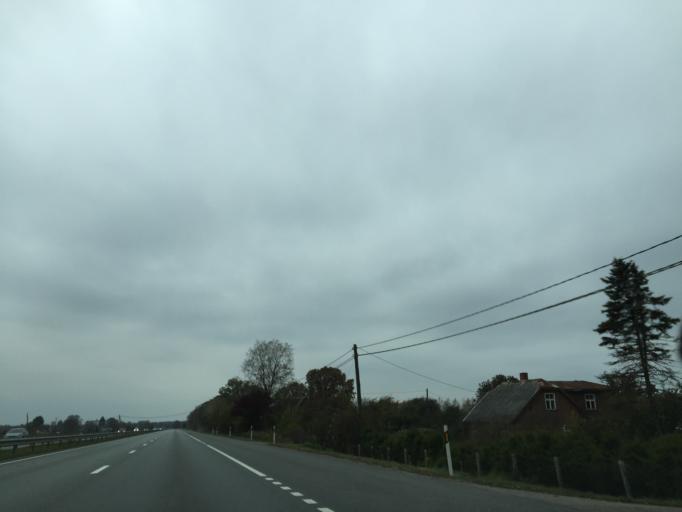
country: LV
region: Olaine
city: Olaine
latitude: 56.7810
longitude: 23.9439
